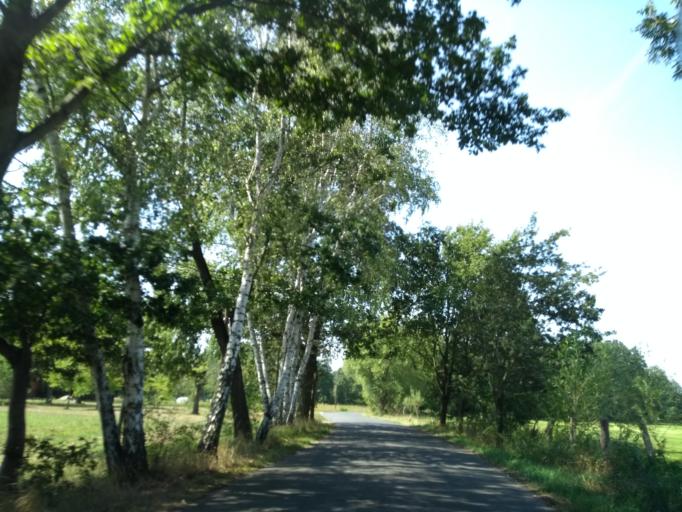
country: DE
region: Brandenburg
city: Burg
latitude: 51.8505
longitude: 14.1247
